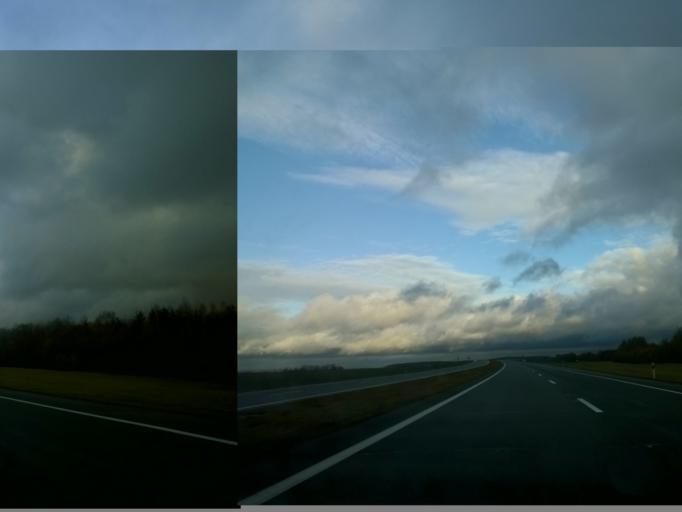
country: BY
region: Brest
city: Baranovichi
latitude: 53.2143
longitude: 26.1345
